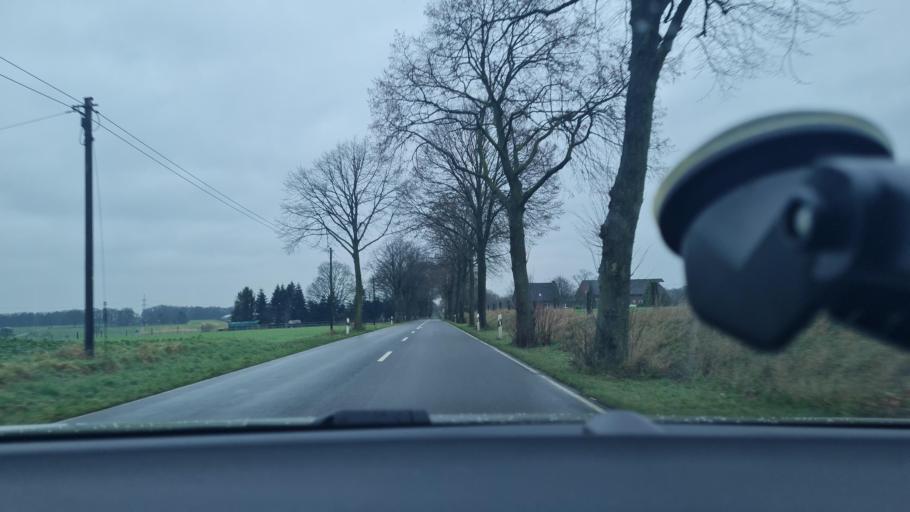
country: DE
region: North Rhine-Westphalia
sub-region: Regierungsbezirk Dusseldorf
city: Hunxe
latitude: 51.7071
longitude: 6.7472
